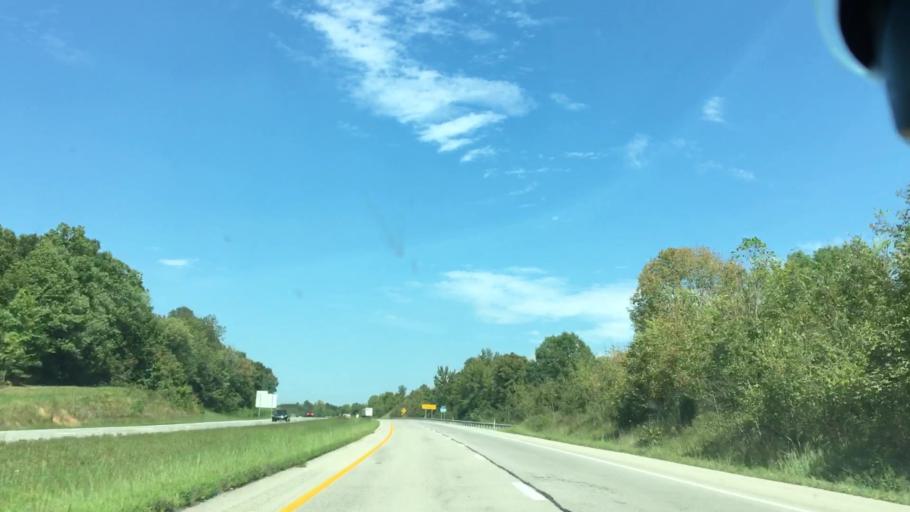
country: US
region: Kentucky
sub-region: Hopkins County
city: Nortonville
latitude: 37.1963
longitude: -87.4402
